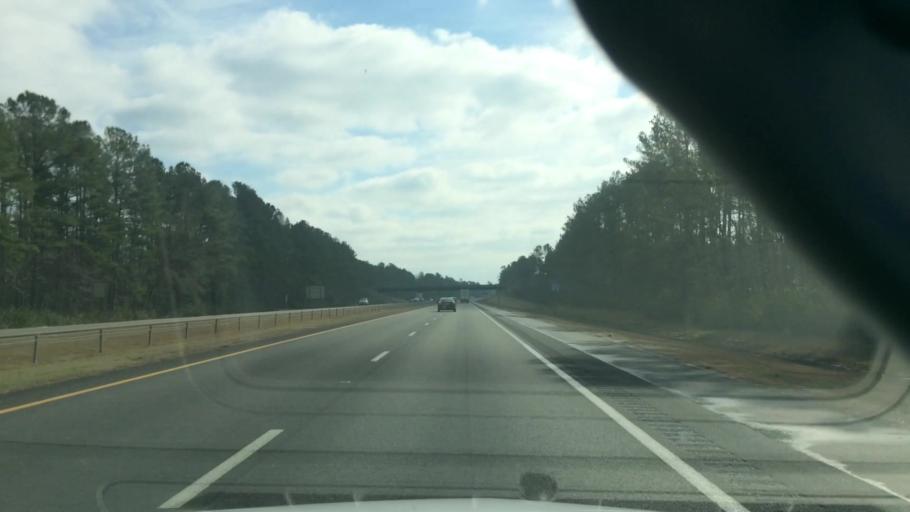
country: US
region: North Carolina
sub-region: Pender County
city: Burgaw
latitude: 34.5690
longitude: -77.8991
